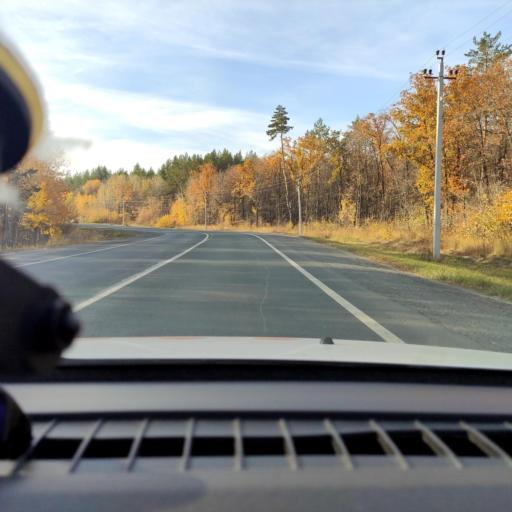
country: RU
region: Samara
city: Volzhskiy
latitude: 53.4482
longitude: 50.1231
